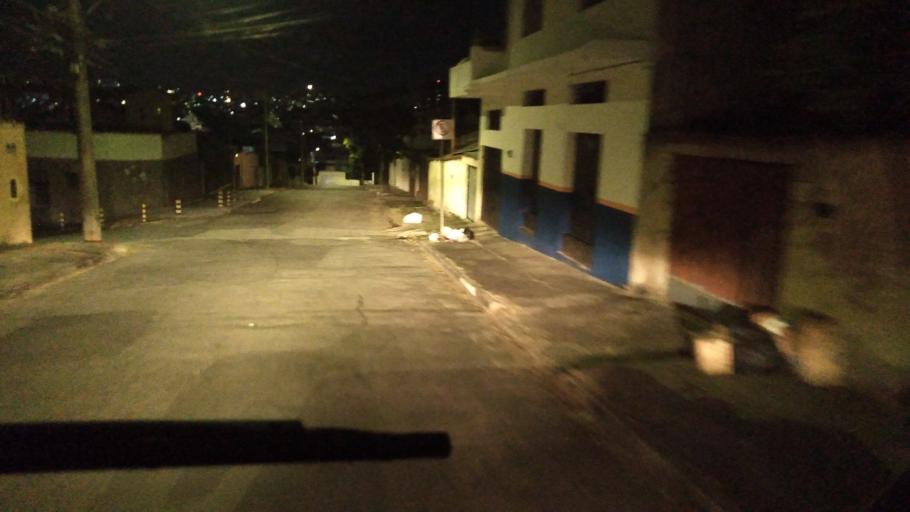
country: BR
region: Minas Gerais
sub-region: Belo Horizonte
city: Belo Horizonte
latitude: -19.8734
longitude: -43.9406
